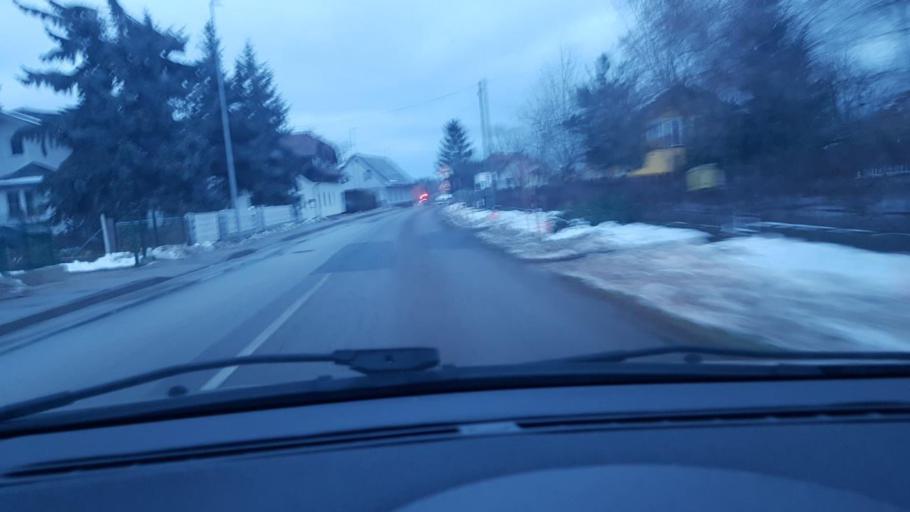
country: SI
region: Hajdina
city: Spodnja Hajdina
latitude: 46.4048
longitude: 15.8371
